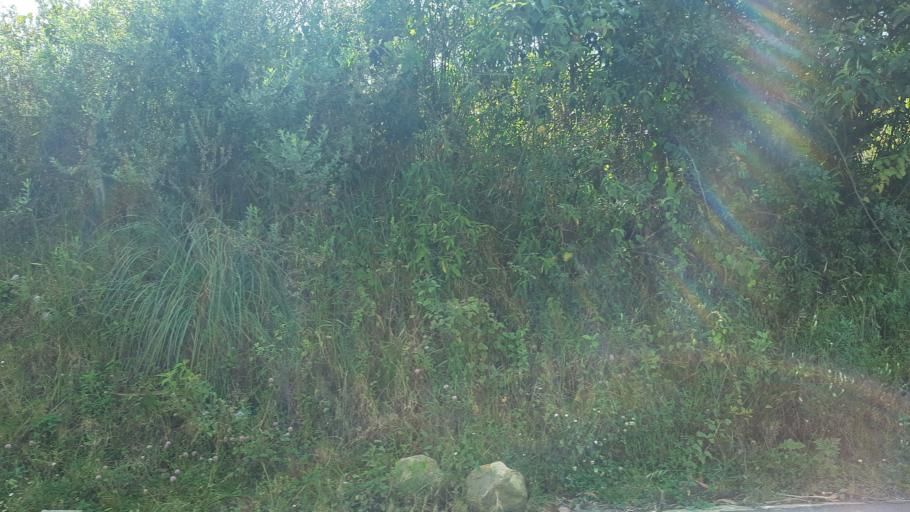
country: CO
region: Boyaca
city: Santa Sofia
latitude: 5.7754
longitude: -73.6053
